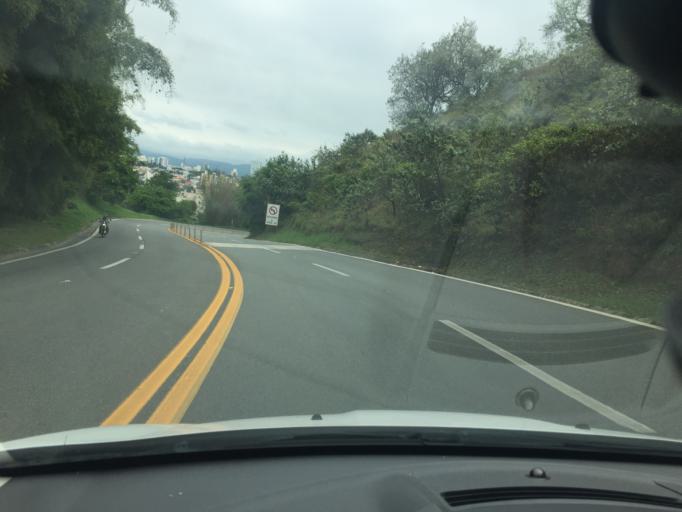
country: BR
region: Sao Paulo
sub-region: Jundiai
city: Jundiai
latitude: -23.1694
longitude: -46.8799
